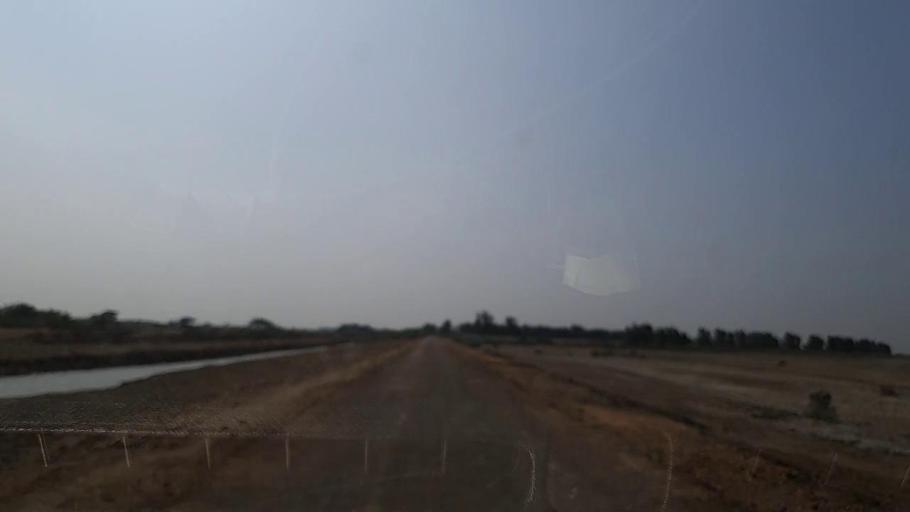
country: PK
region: Sindh
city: Mirpur Sakro
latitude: 24.5298
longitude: 67.7778
